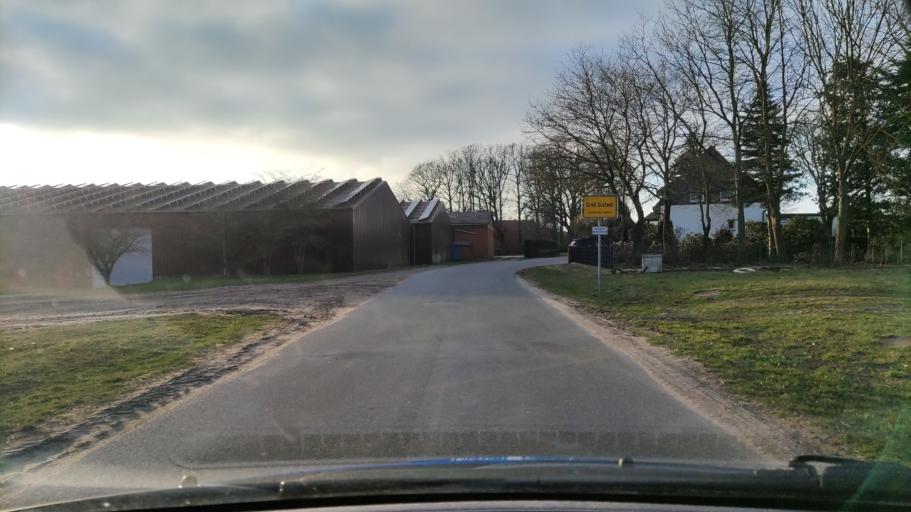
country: DE
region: Lower Saxony
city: Gerdau
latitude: 52.9707
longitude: 10.4018
